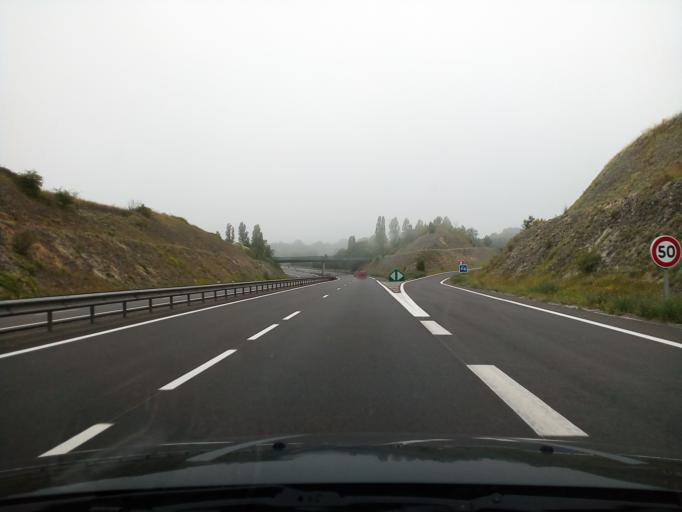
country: FR
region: Poitou-Charentes
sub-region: Departement de la Charente
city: Chassors
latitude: 45.6688
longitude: -0.2078
